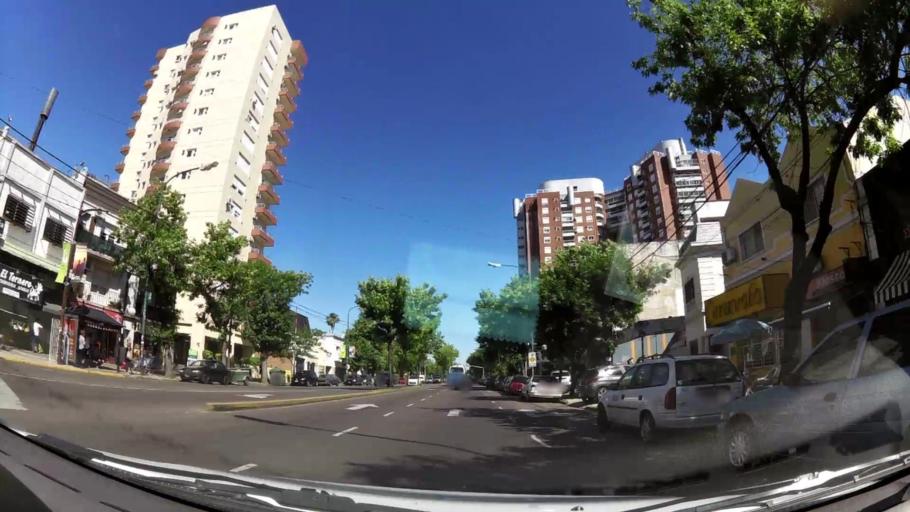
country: AR
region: Buenos Aires
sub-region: Partido de San Isidro
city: San Isidro
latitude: -34.4618
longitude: -58.5265
